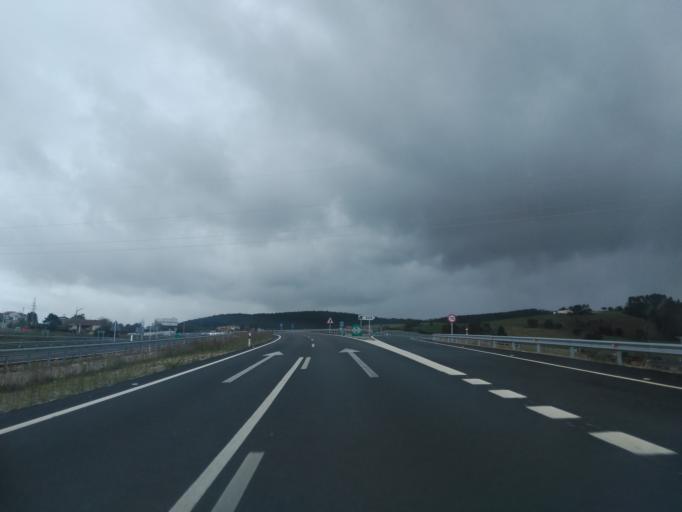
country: ES
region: Cantabria
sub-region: Provincia de Cantabria
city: Polanco
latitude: 43.3426
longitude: -3.9918
